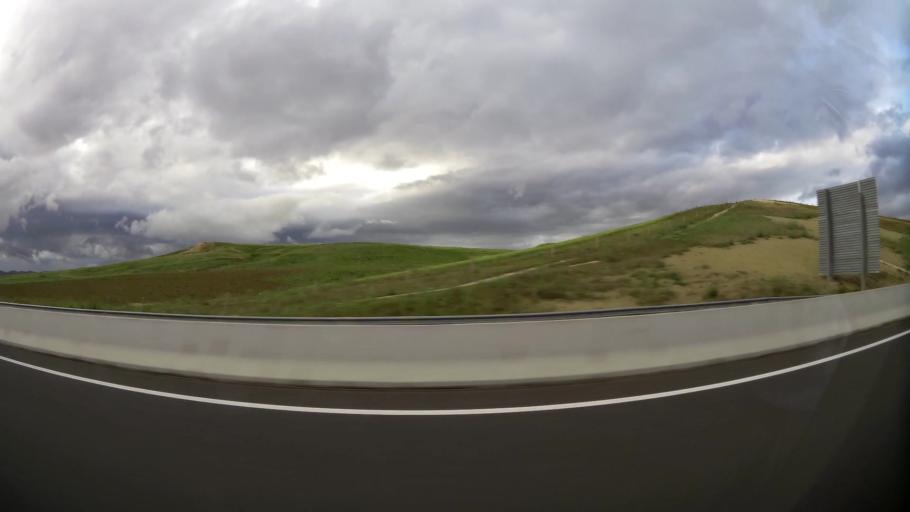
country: MA
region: Taza-Al Hoceima-Taounate
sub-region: Taza
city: Taza
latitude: 34.2513
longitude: -3.9014
